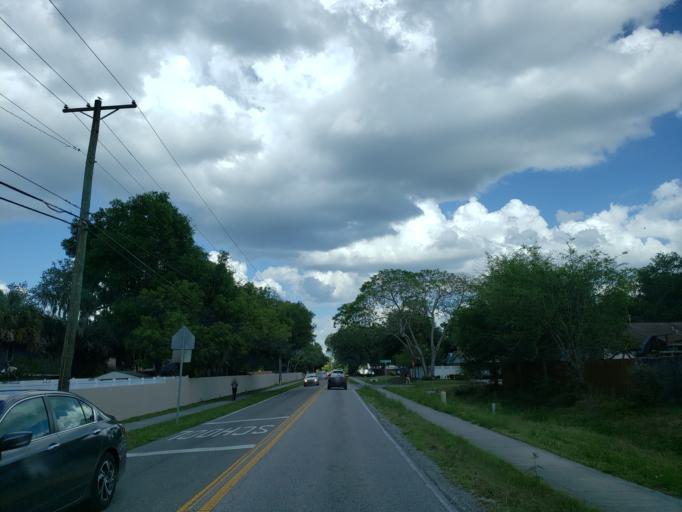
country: US
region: Florida
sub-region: Hillsborough County
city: Mango
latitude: 27.9597
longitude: -82.3007
